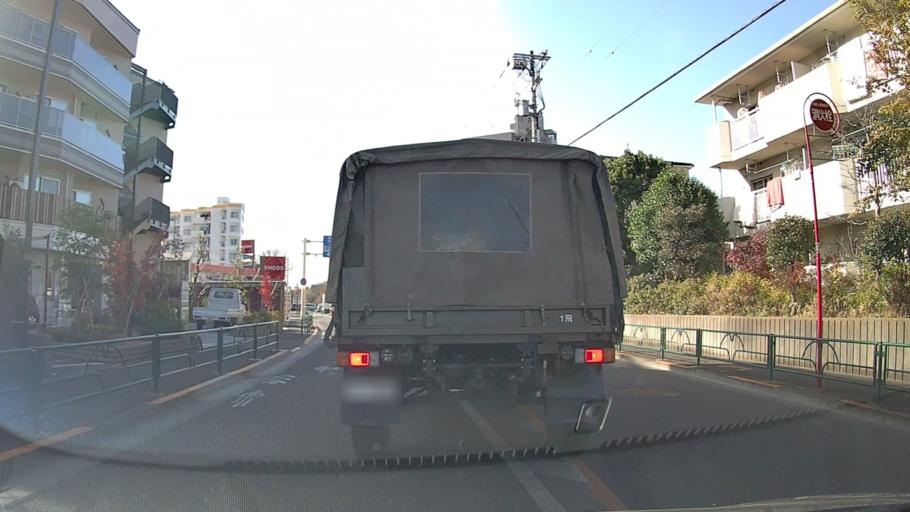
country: JP
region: Tokyo
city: Musashino
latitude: 35.7286
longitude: 139.6098
